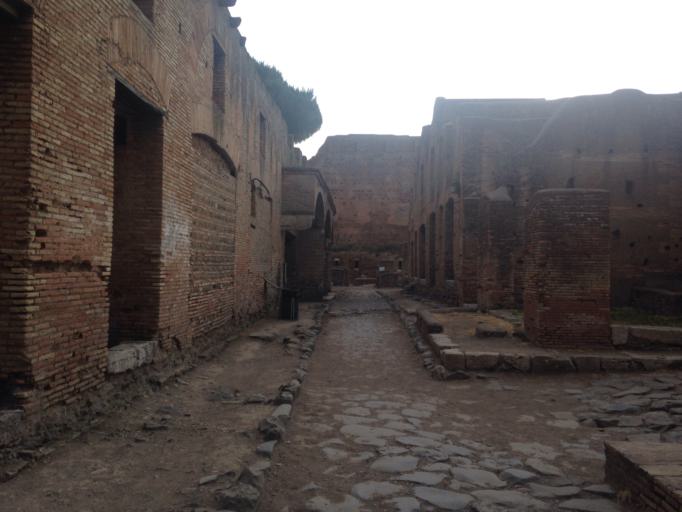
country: IT
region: Latium
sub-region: Citta metropolitana di Roma Capitale
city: Lido di Ostia
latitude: 41.7547
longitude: 12.2887
